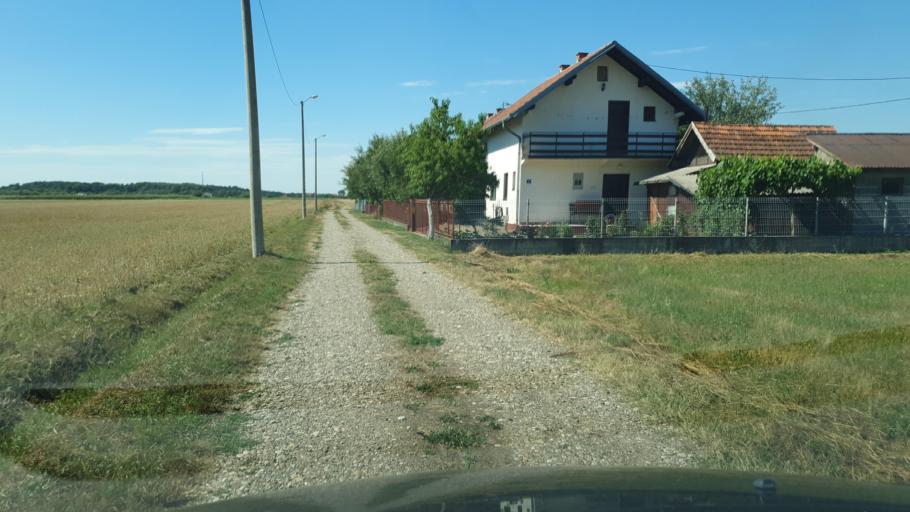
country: BA
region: Republika Srpska
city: Bijeljina
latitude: 44.7227
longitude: 19.1985
